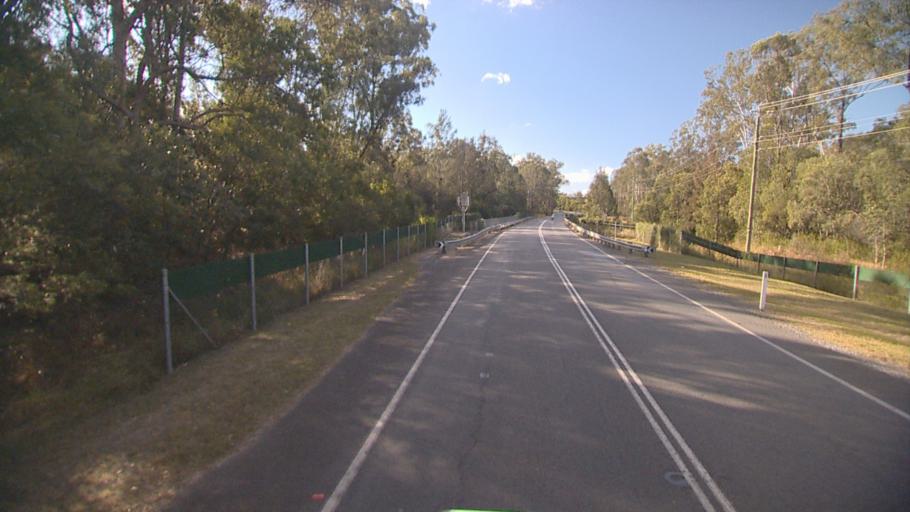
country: AU
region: Queensland
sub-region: Logan
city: North Maclean
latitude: -27.8046
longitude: 152.9826
